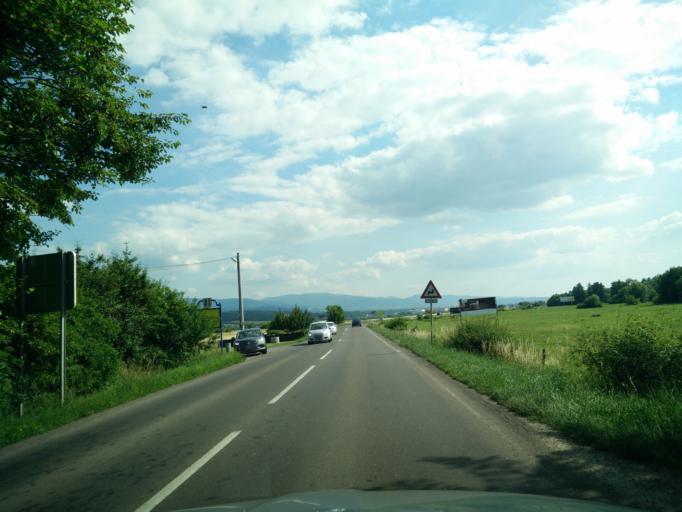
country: SK
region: Nitriansky
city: Prievidza
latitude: 48.8132
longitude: 18.6427
